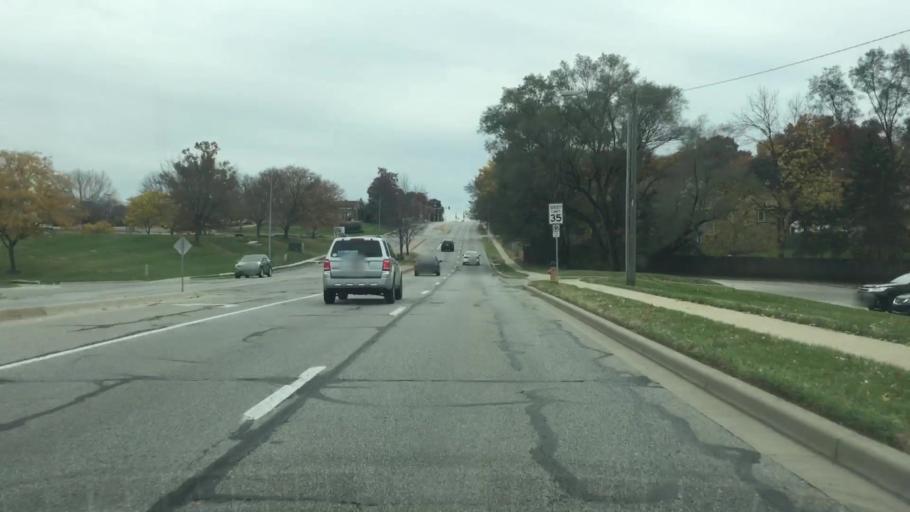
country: US
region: Kansas
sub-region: Johnson County
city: Merriam
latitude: 38.9967
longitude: -94.7238
